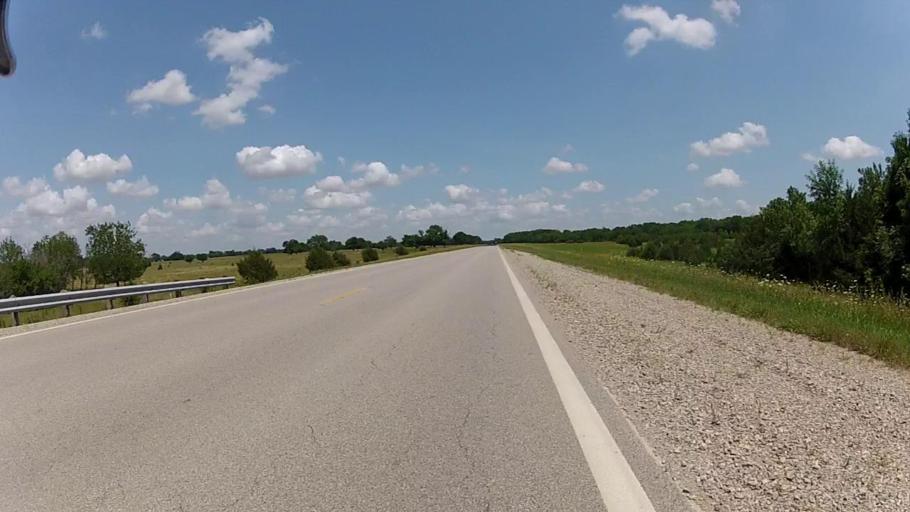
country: US
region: Kansas
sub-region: Labette County
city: Altamont
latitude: 37.1941
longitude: -95.3951
